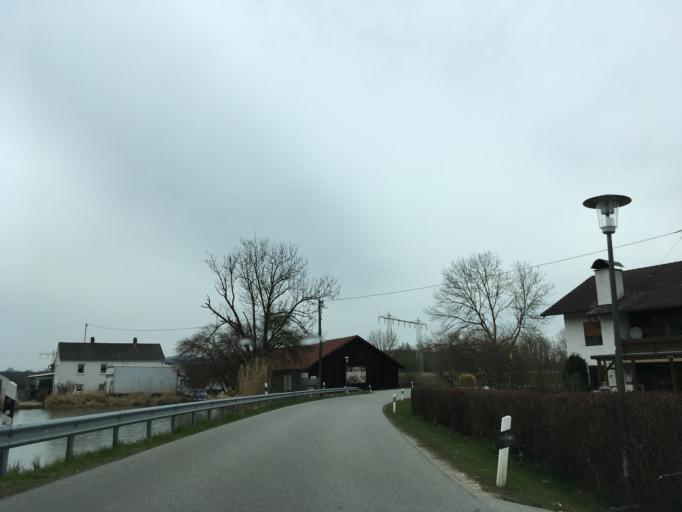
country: DE
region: Bavaria
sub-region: Upper Bavaria
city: Jettenbach
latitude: 48.1710
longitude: 12.3821
